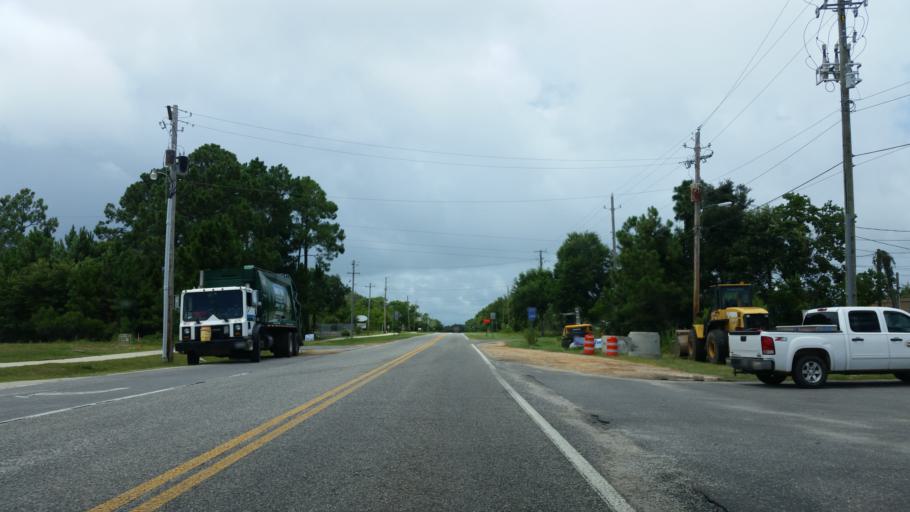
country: US
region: Florida
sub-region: Santa Rosa County
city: Woodlawn Beach
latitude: 30.4002
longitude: -86.9998
